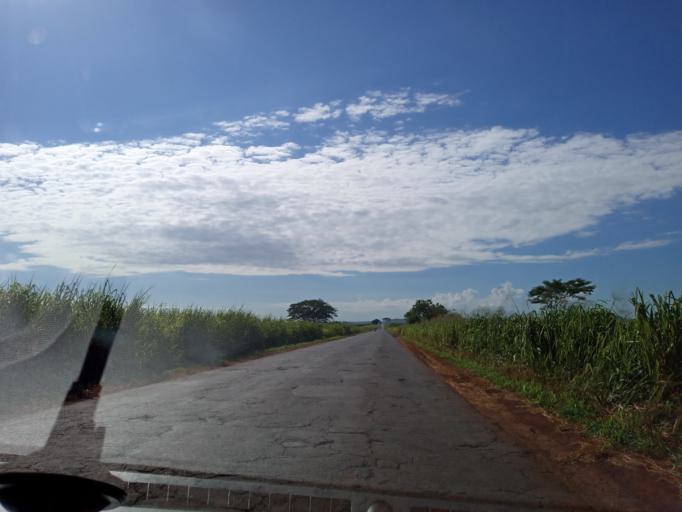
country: BR
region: Goias
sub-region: Itumbiara
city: Itumbiara
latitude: -18.4463
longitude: -49.1707
